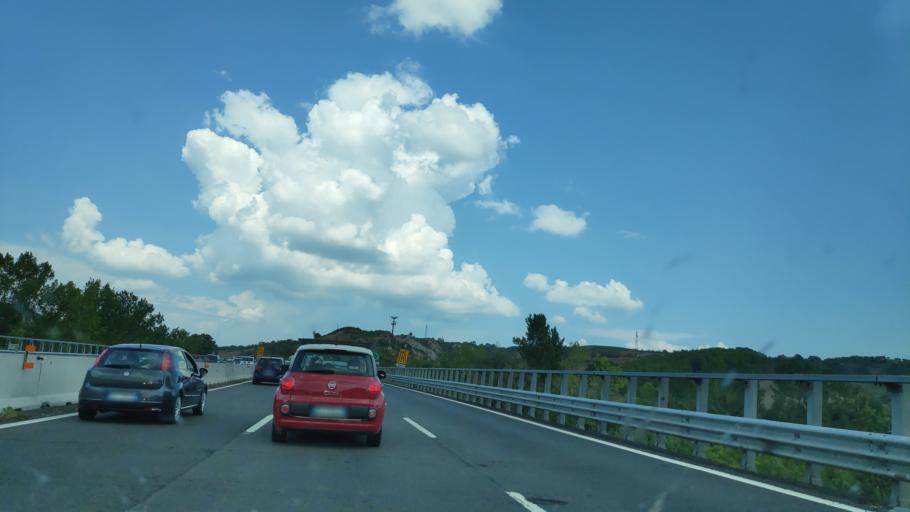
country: IT
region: Umbria
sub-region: Provincia di Terni
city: Ficulle
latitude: 42.8269
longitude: 12.0421
